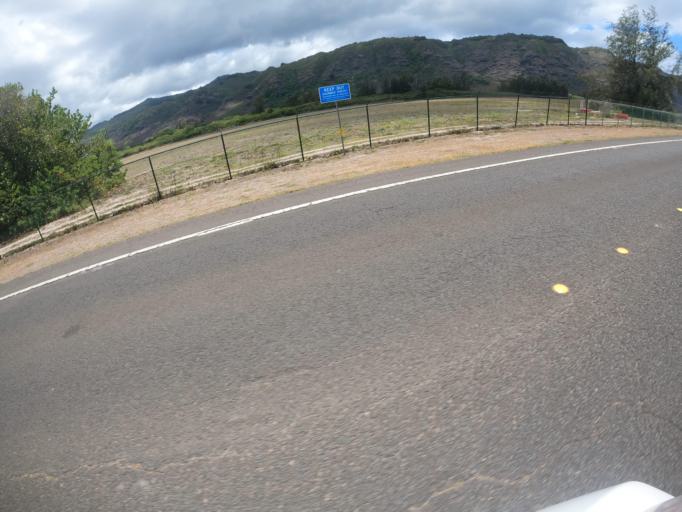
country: US
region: Hawaii
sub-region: Honolulu County
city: Mokuleia
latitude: 21.5812
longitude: -158.1954
